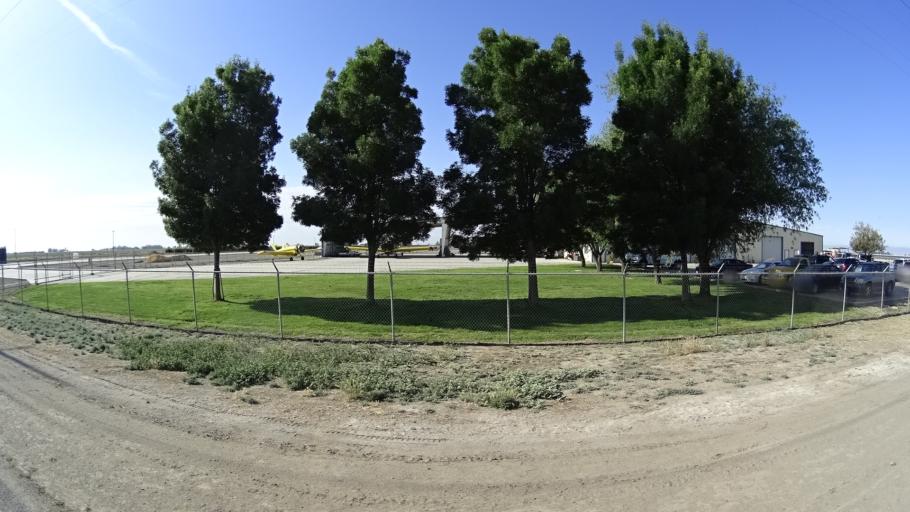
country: US
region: California
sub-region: Kings County
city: Stratford
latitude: 36.2259
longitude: -119.7999
